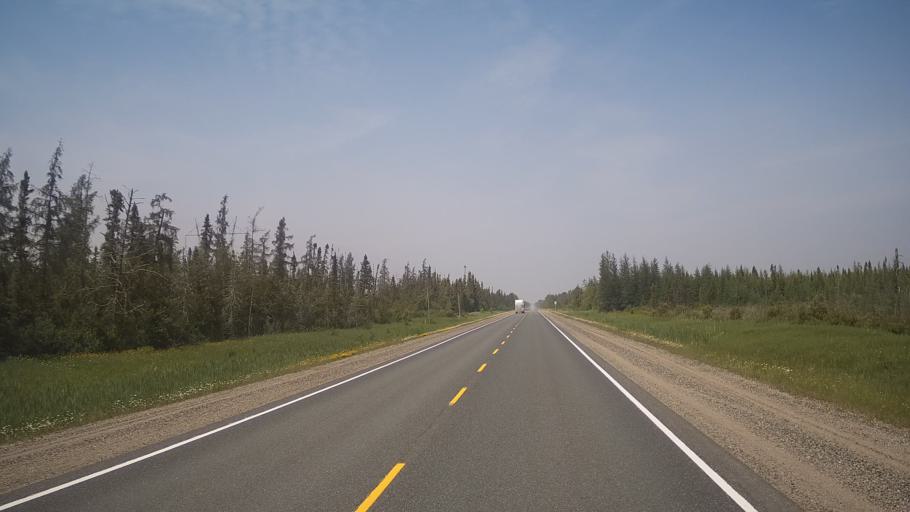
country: CA
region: Ontario
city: Timmins
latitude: 48.7915
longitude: -81.3660
